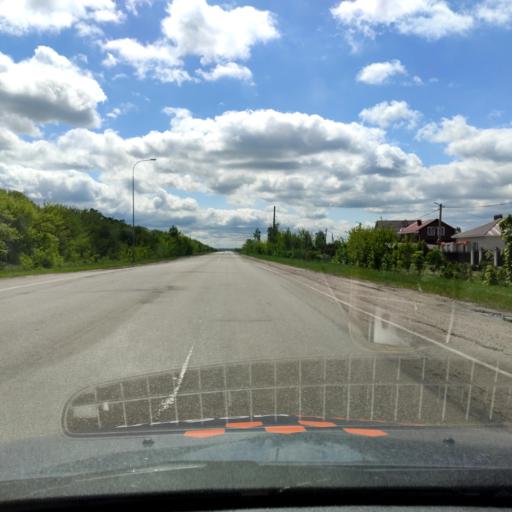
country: RU
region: Voronezj
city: Novaya Usman'
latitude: 51.6190
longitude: 39.3360
